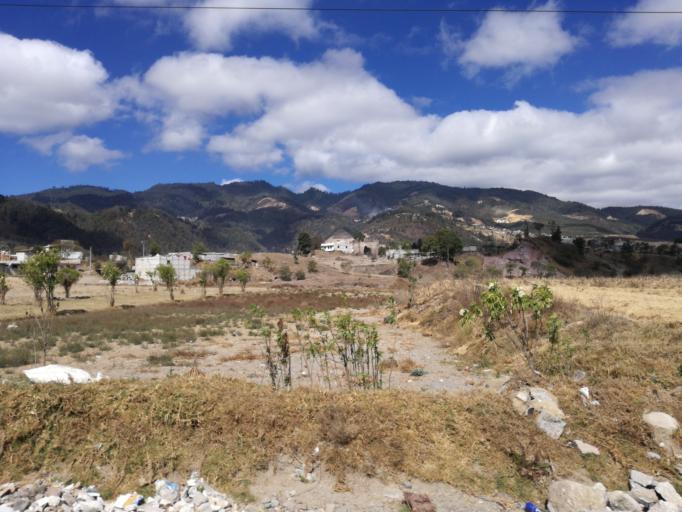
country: GT
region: Quetzaltenango
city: Quetzaltenango
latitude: 14.8021
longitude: -91.5425
